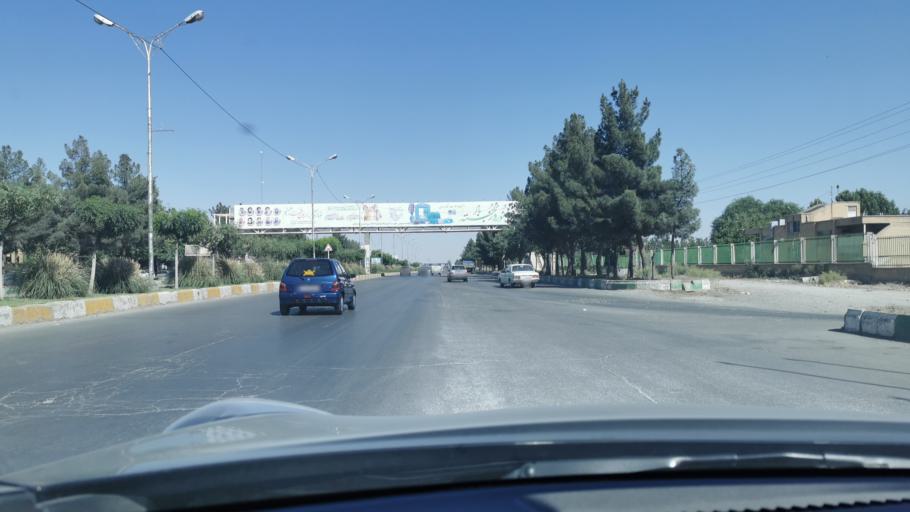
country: IR
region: Razavi Khorasan
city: Chenaran
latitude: 36.6376
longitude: 59.1241
